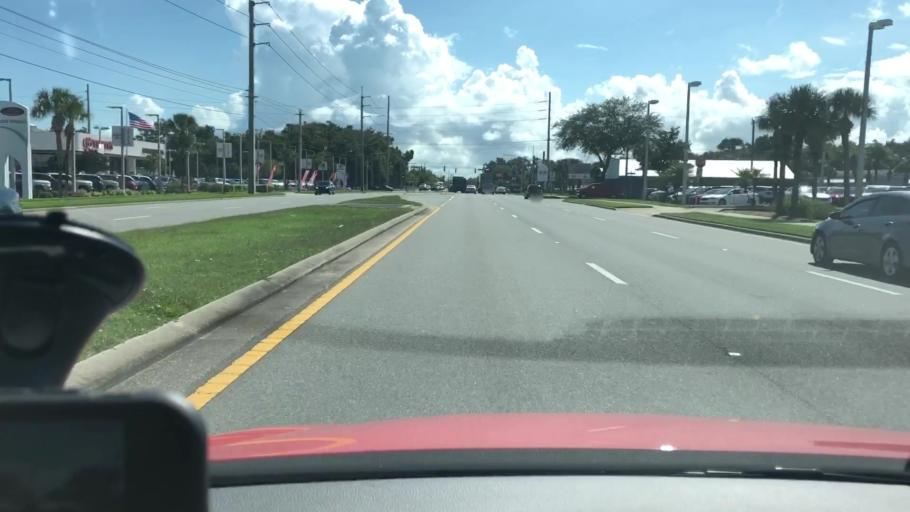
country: US
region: Florida
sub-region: Volusia County
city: Daytona Beach
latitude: 29.2128
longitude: -81.0449
